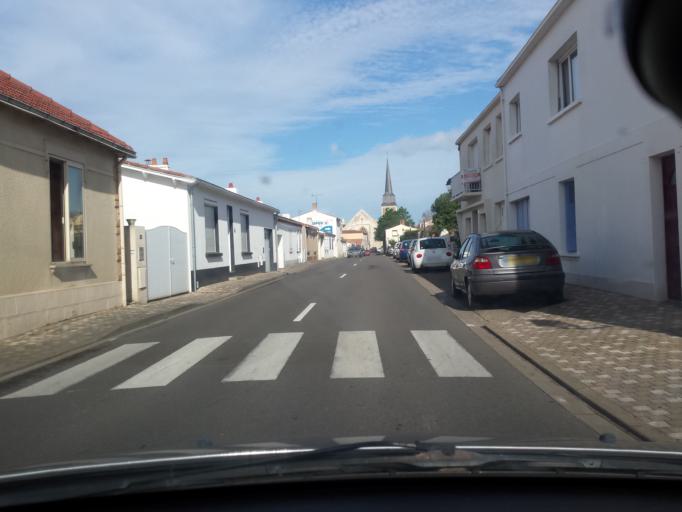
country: FR
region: Pays de la Loire
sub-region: Departement de la Vendee
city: Olonne-sur-Mer
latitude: 46.5358
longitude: -1.7701
